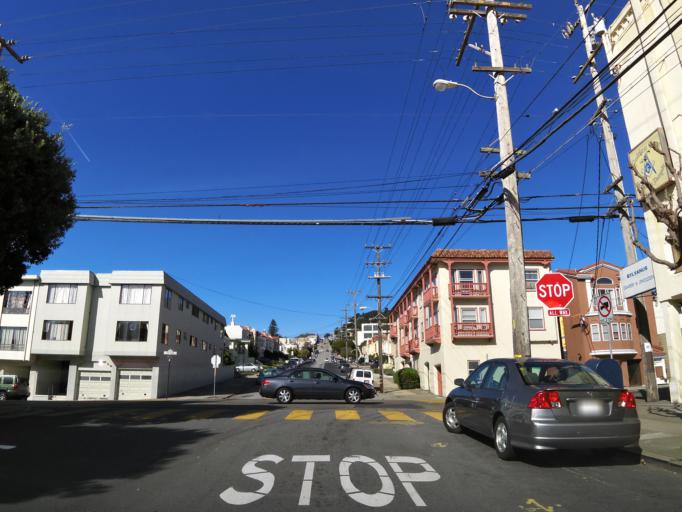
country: US
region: California
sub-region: San Mateo County
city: Daly City
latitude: 37.7431
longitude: -122.4702
